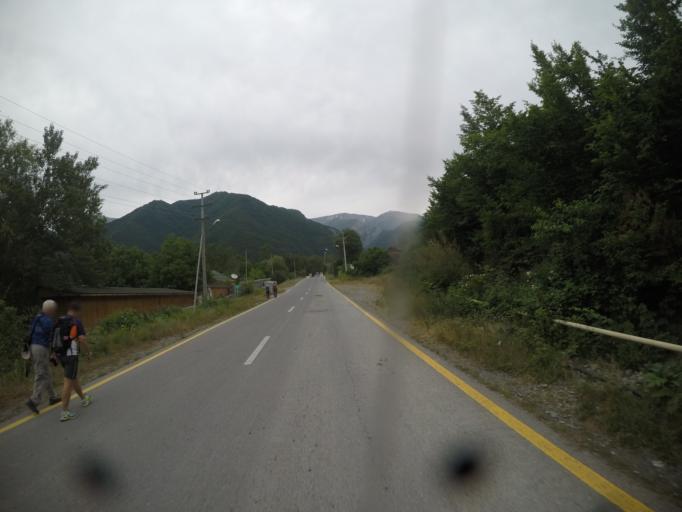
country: AZ
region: Shaki City
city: Sheki
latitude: 41.2520
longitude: 47.2068
